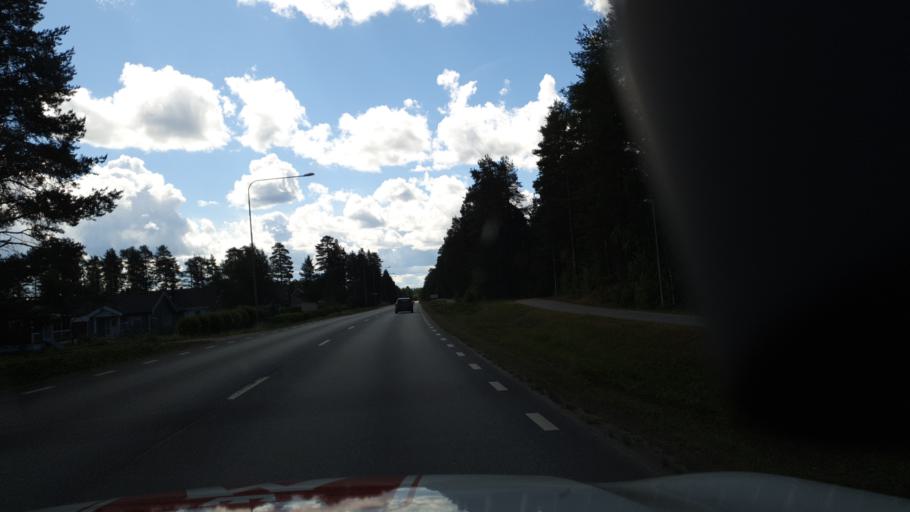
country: SE
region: Vaesterbotten
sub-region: Lycksele Kommun
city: Lycksele
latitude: 64.6021
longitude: 18.7006
